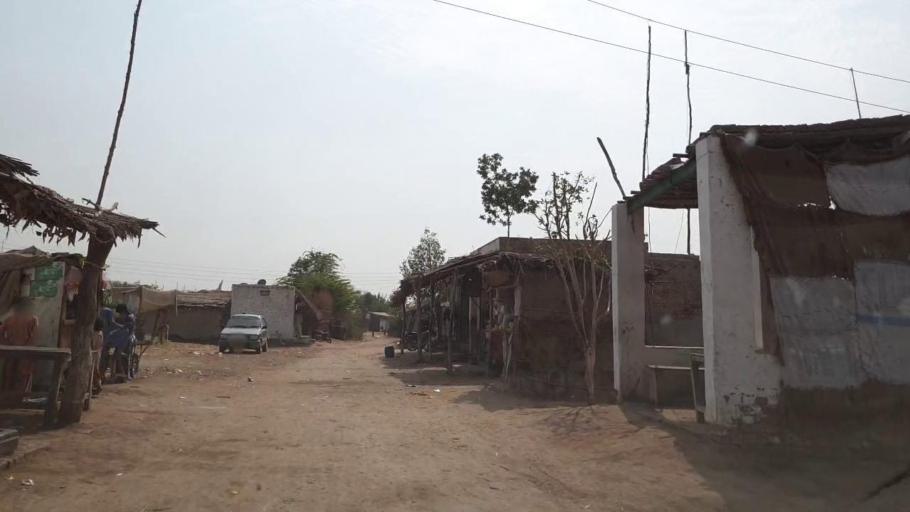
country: PK
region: Sindh
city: Mirpur Khas
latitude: 25.5376
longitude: 69.0930
